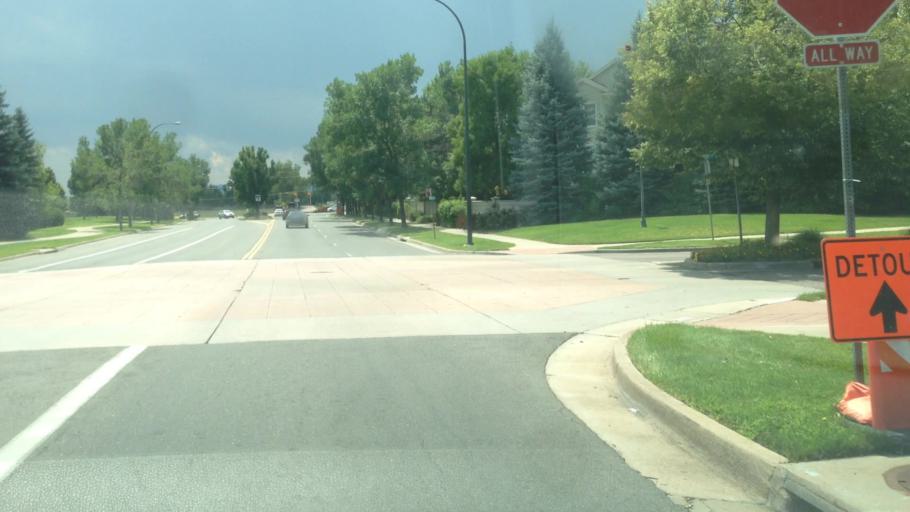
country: US
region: Colorado
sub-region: Jefferson County
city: Columbine
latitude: 39.6118
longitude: -105.0571
